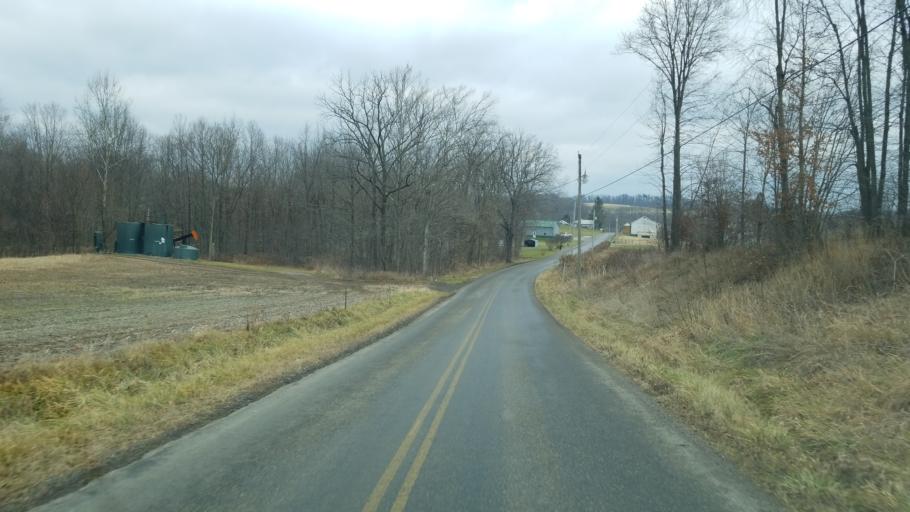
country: US
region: Ohio
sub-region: Holmes County
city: Millersburg
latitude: 40.5925
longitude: -81.9692
